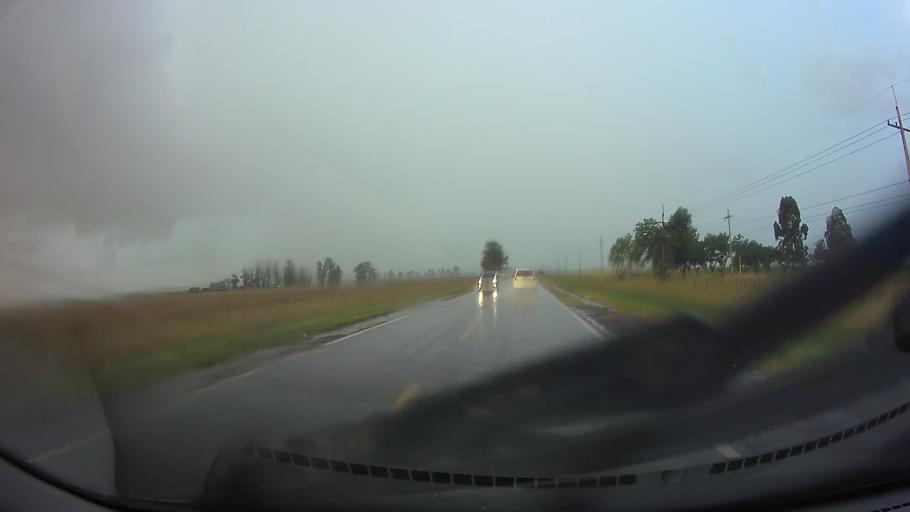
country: PY
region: Paraguari
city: Paraguari
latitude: -25.6619
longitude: -57.1621
